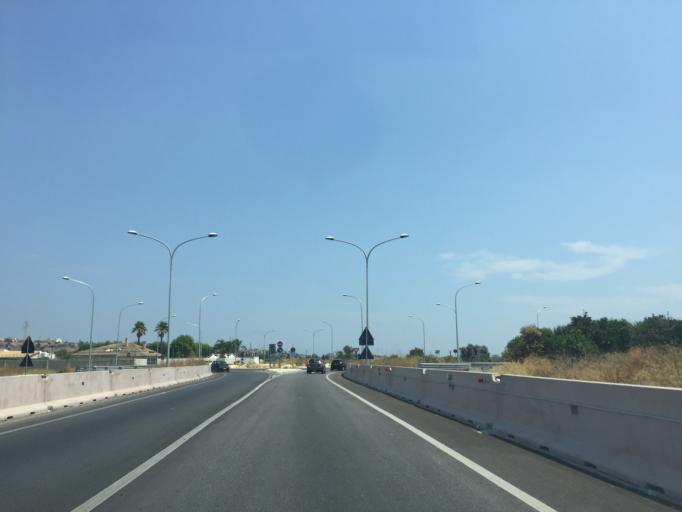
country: IT
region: Sicily
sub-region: Provincia di Siracusa
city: Belvedere
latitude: 37.0728
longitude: 15.2361
